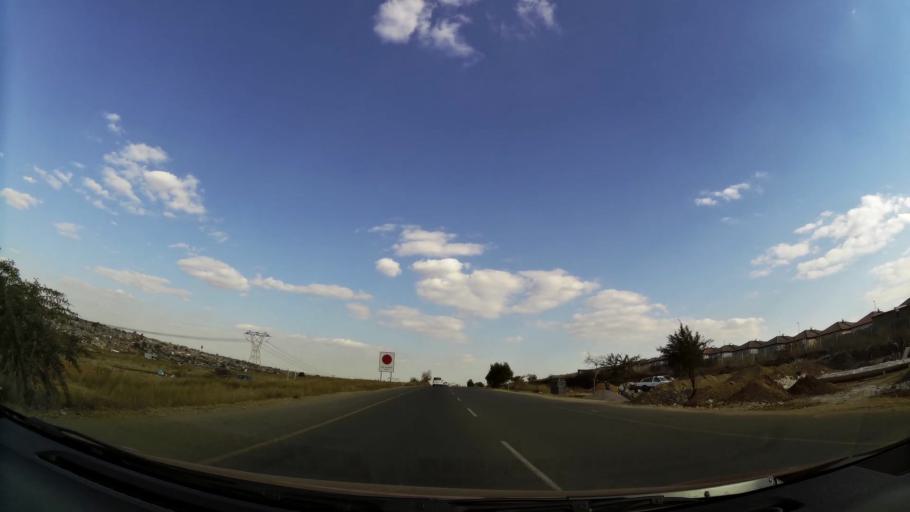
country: ZA
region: Gauteng
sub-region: Ekurhuleni Metropolitan Municipality
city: Tembisa
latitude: -25.9814
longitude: 28.1939
